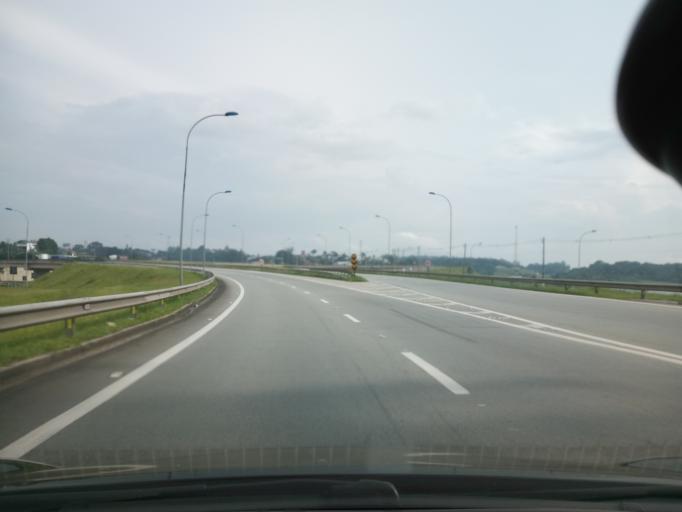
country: BR
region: Sao Paulo
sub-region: Sao Bernardo Do Campo
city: Sao Bernardo do Campo
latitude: -23.7620
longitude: -46.5939
